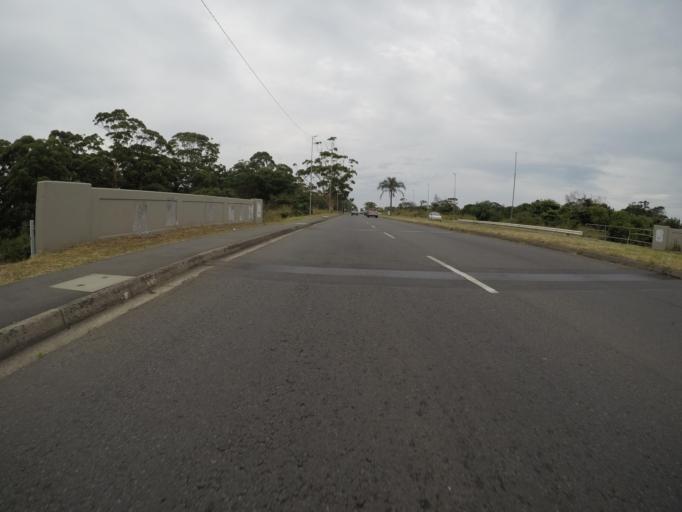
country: ZA
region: Eastern Cape
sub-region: Buffalo City Metropolitan Municipality
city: East London
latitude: -32.9973
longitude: 27.8820
